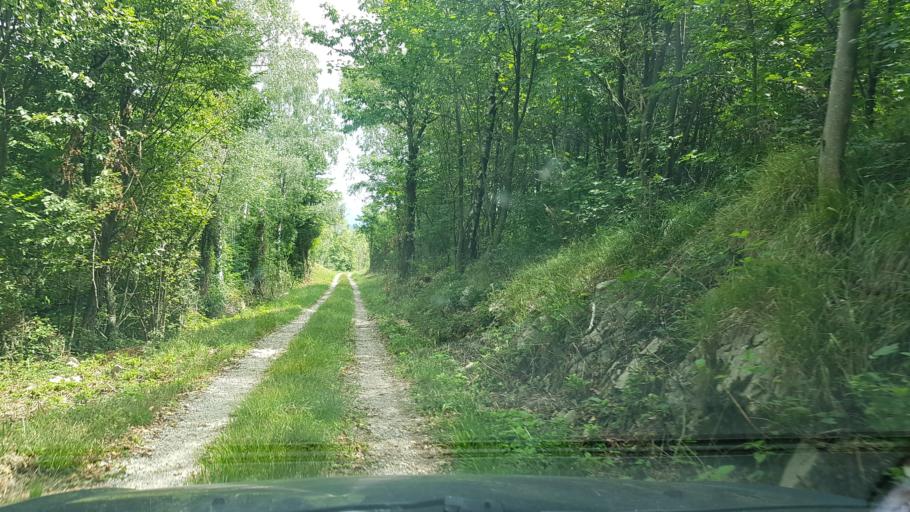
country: SI
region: Kanal
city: Deskle
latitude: 46.0153
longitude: 13.6366
